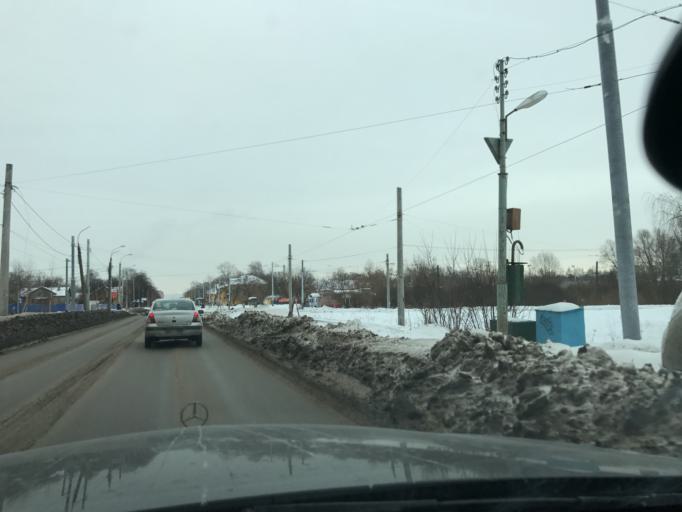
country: RU
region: Nizjnij Novgorod
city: Gorbatovka
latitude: 56.2453
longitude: 43.8241
